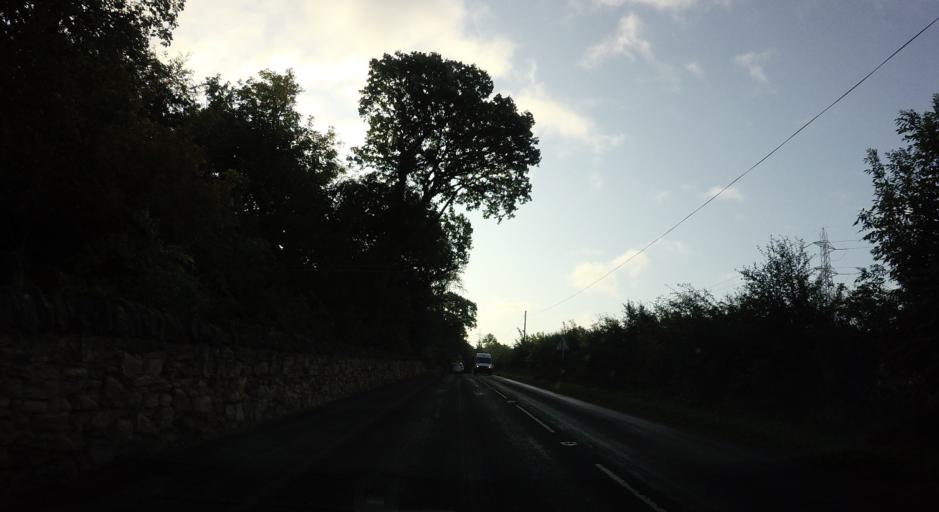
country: GB
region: Scotland
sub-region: East Lothian
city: Musselburgh
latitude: 55.9114
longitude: -3.0192
